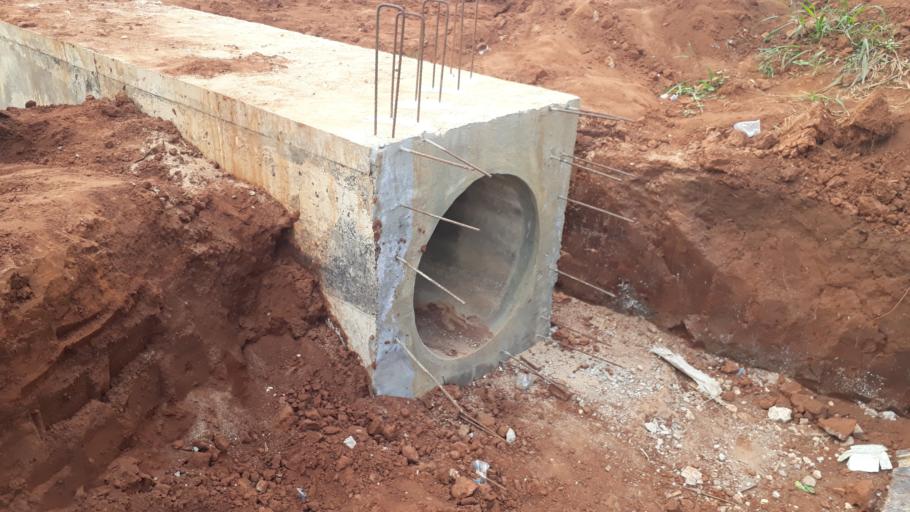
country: NG
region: Abia
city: Umuahia
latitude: 5.4790
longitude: 7.3287
